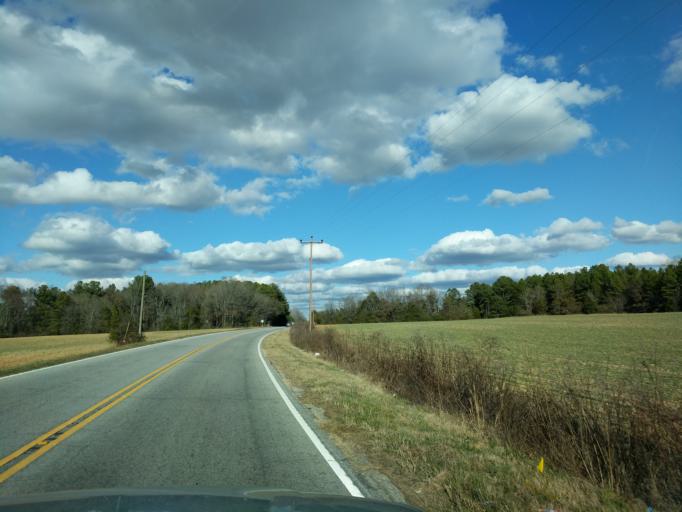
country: US
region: South Carolina
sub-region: Laurens County
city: Laurens
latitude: 34.4090
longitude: -82.0514
